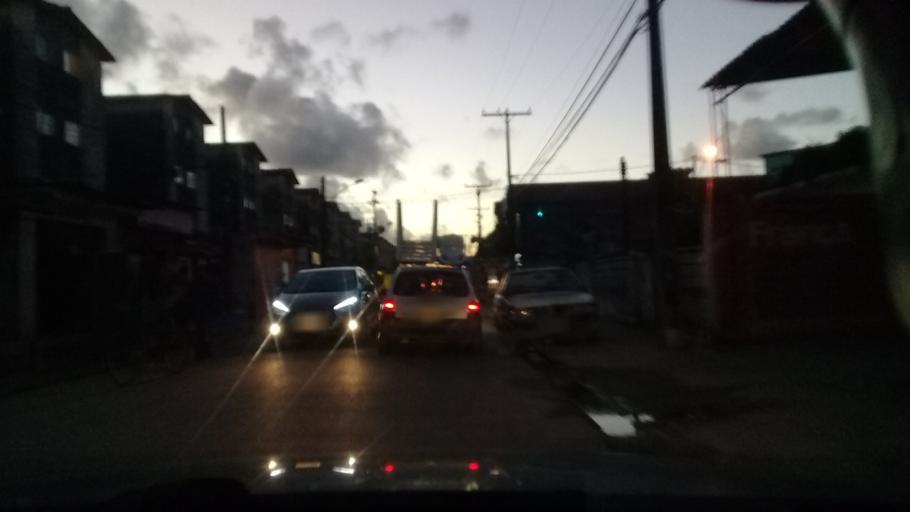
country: BR
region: Pernambuco
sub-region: Recife
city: Recife
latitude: -8.1133
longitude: -34.9179
